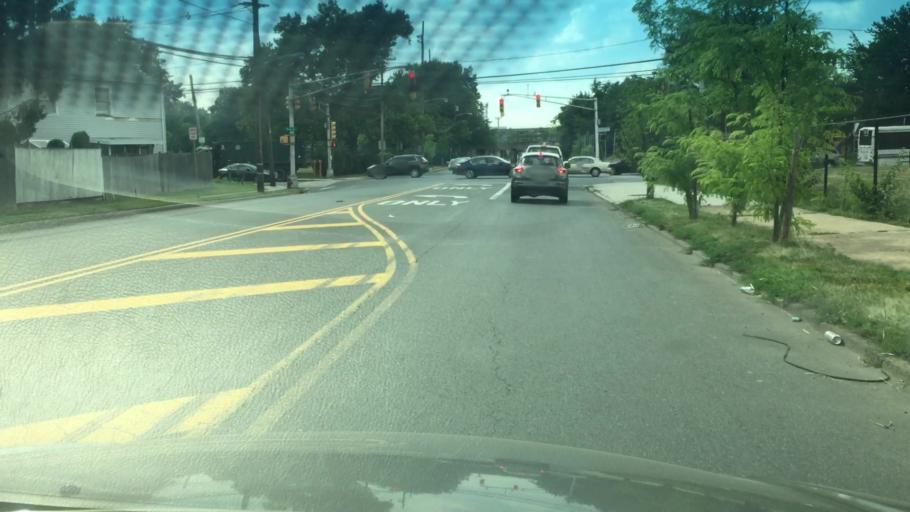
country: US
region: New Jersey
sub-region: Union County
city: Elizabeth
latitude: 40.6567
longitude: -74.1818
